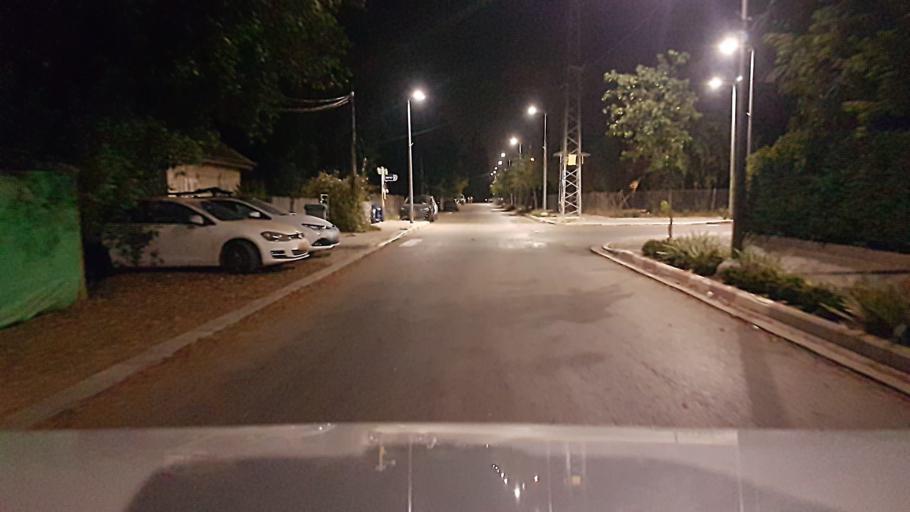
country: IL
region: Central District
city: Nehalim
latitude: 32.0753
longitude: 34.9301
